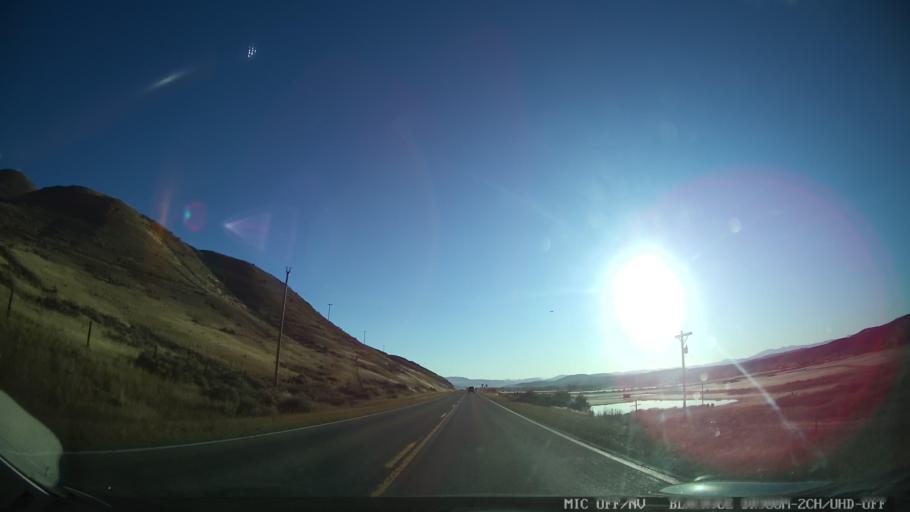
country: US
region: Colorado
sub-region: Grand County
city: Kremmling
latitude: 40.0525
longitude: -106.3419
